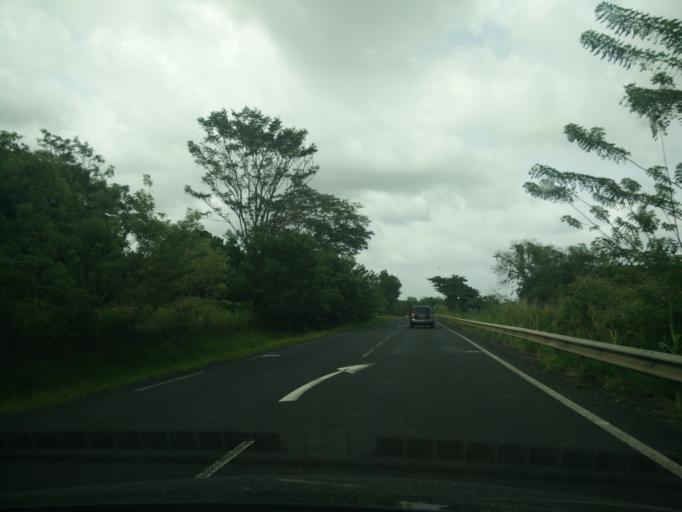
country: GP
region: Guadeloupe
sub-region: Guadeloupe
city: Petit-Bourg
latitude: 16.1971
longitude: -61.6461
